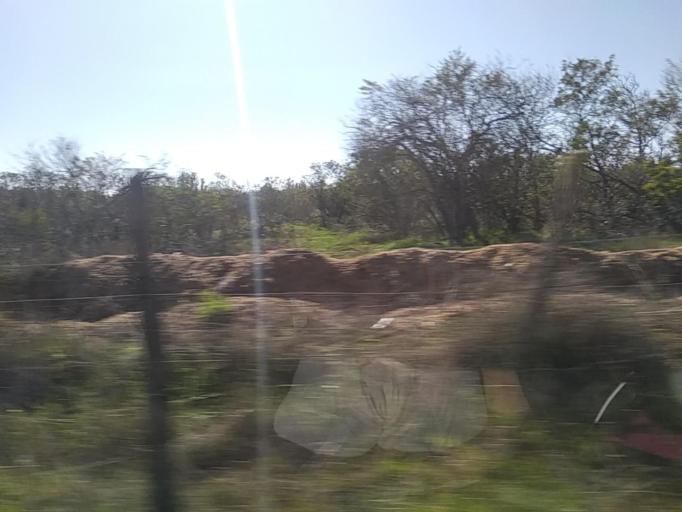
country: CL
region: Valparaiso
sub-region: San Antonio Province
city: El Tabo
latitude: -33.4096
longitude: -71.5960
